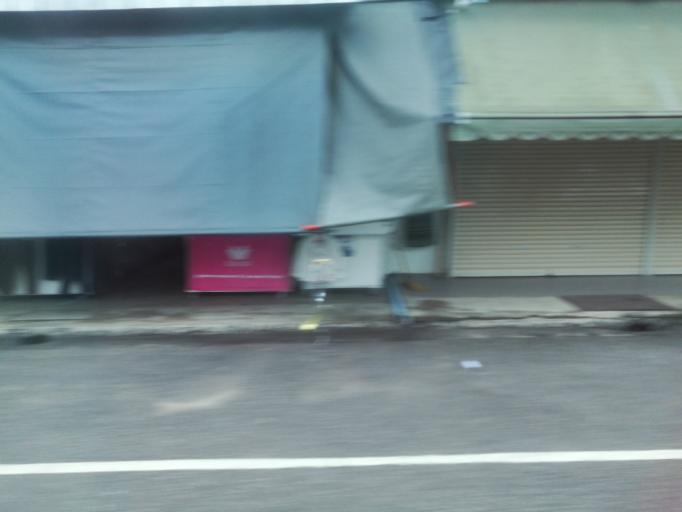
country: TH
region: Prachuap Khiri Khan
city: Prachuap Khiri Khan
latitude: 11.8075
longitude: 99.7959
